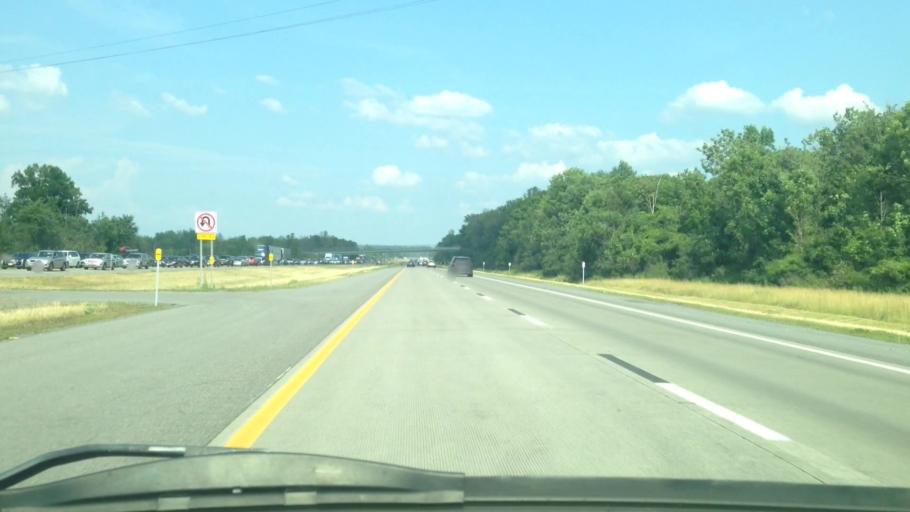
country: US
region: New York
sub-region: Onondaga County
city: Peru
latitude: 43.0856
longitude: -76.4153
